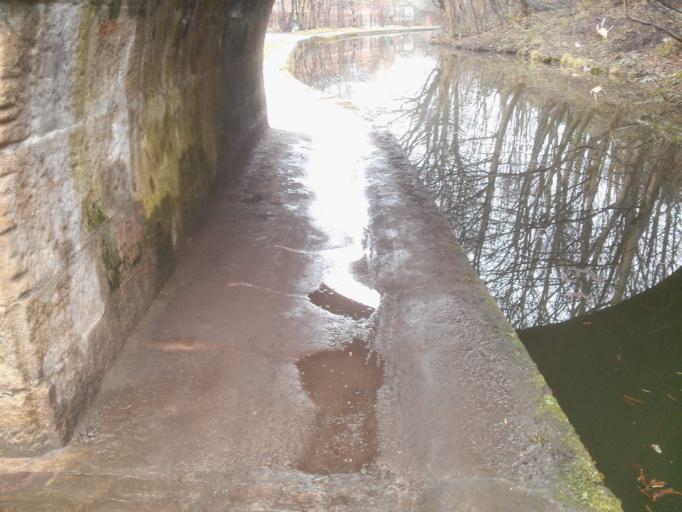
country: GB
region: England
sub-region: City and Borough of Leeds
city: Horsforth
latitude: 53.8151
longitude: -1.6087
